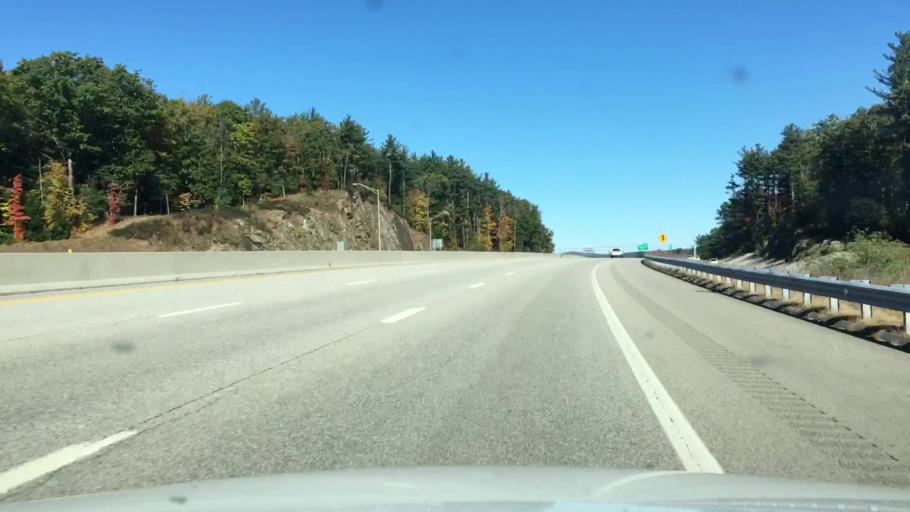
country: US
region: New Hampshire
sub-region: Strafford County
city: Rochester
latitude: 43.2977
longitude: -70.9941
